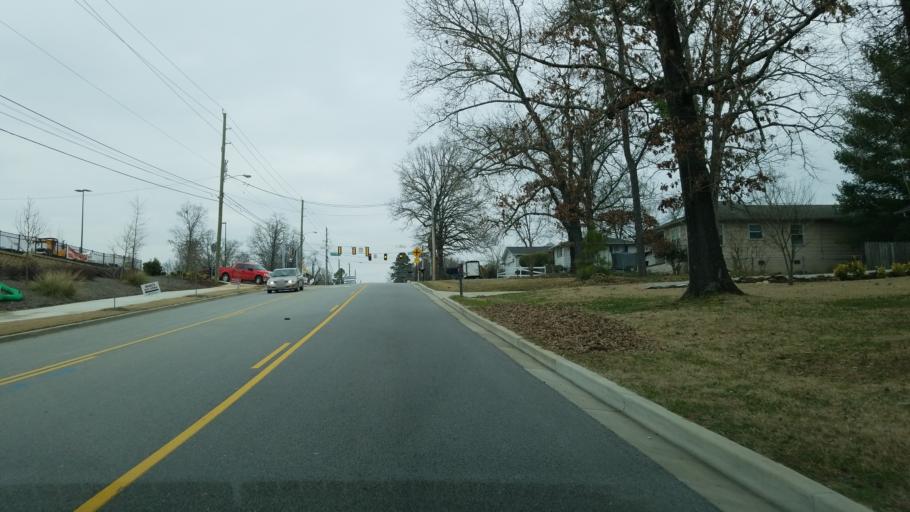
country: US
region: Tennessee
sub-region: Hamilton County
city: East Brainerd
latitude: 35.0423
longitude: -85.1489
